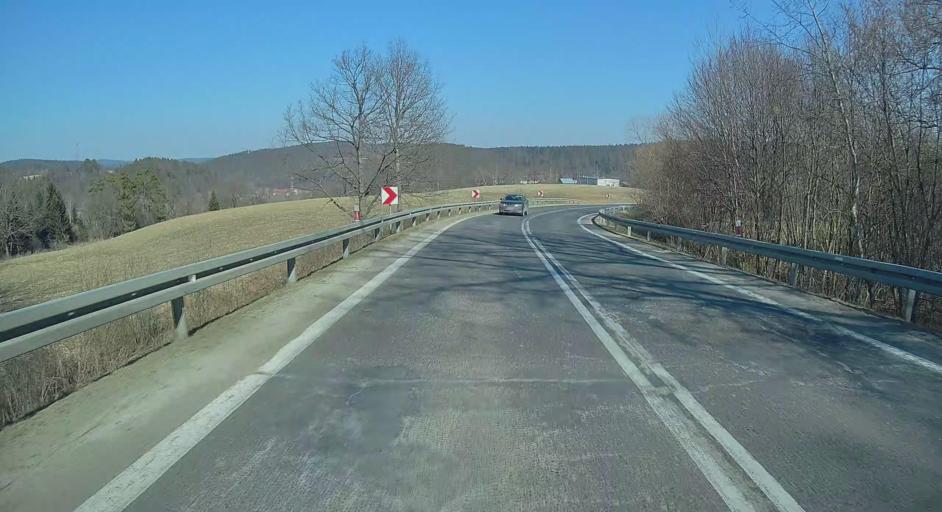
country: PL
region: Subcarpathian Voivodeship
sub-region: Powiat przemyski
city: Bircza
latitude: 49.6548
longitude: 22.4257
